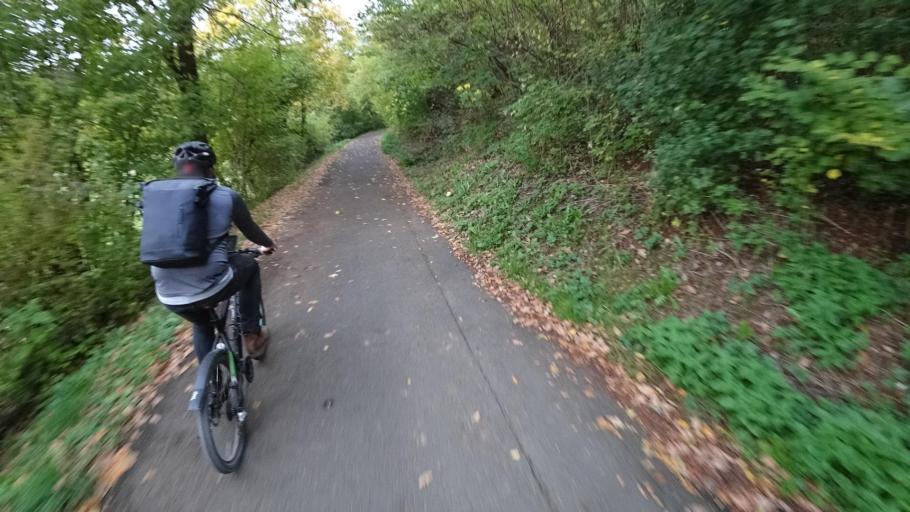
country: DE
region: Rheinland-Pfalz
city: Remagen
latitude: 50.5488
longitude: 7.1986
